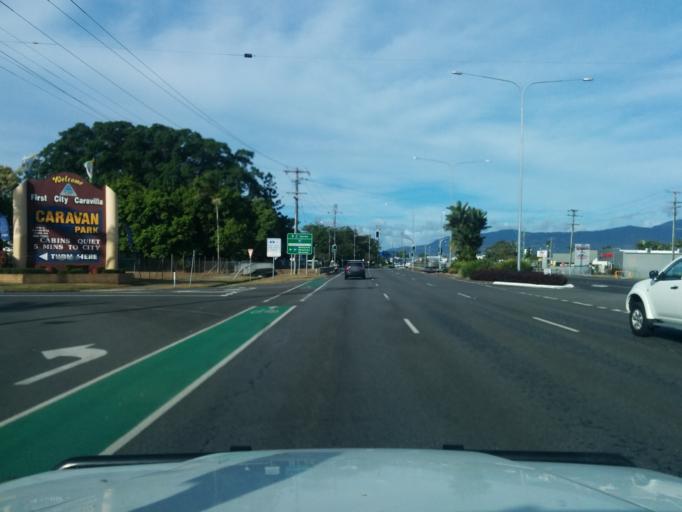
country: AU
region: Queensland
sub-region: Cairns
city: Woree
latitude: -16.9394
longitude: 145.7437
